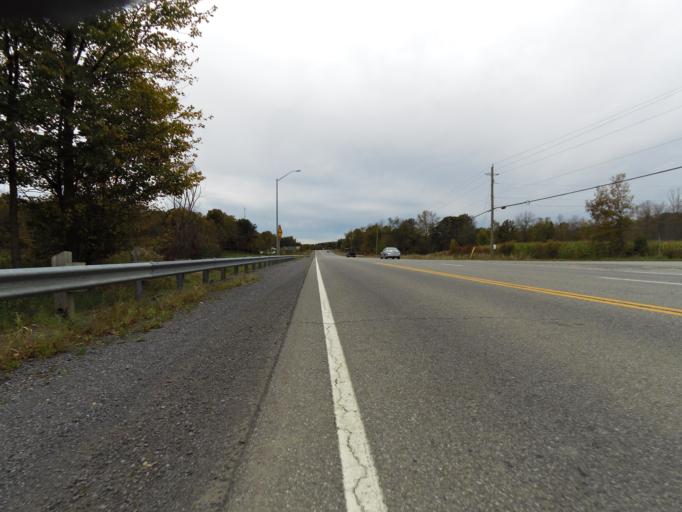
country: CA
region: Ontario
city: Gananoque
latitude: 44.4320
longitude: -76.2905
